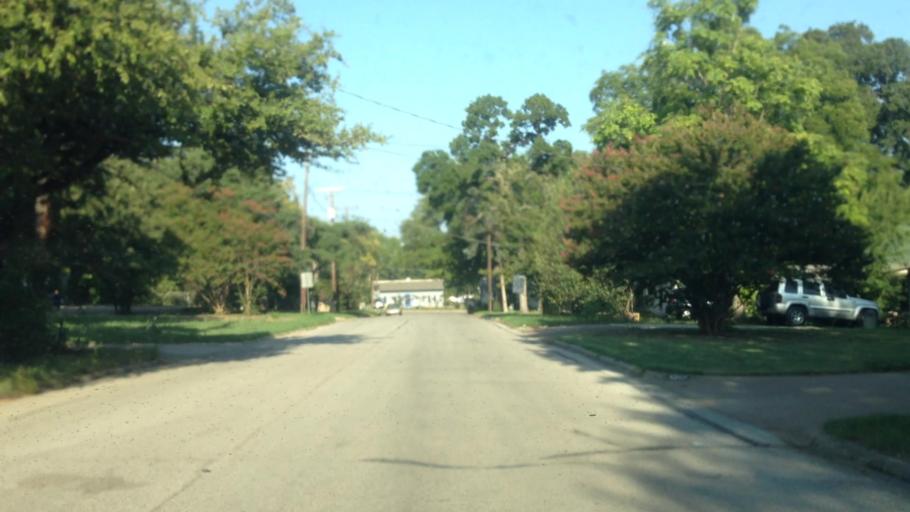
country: US
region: Texas
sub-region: Tarrant County
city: Haltom City
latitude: 32.7999
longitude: -97.2574
